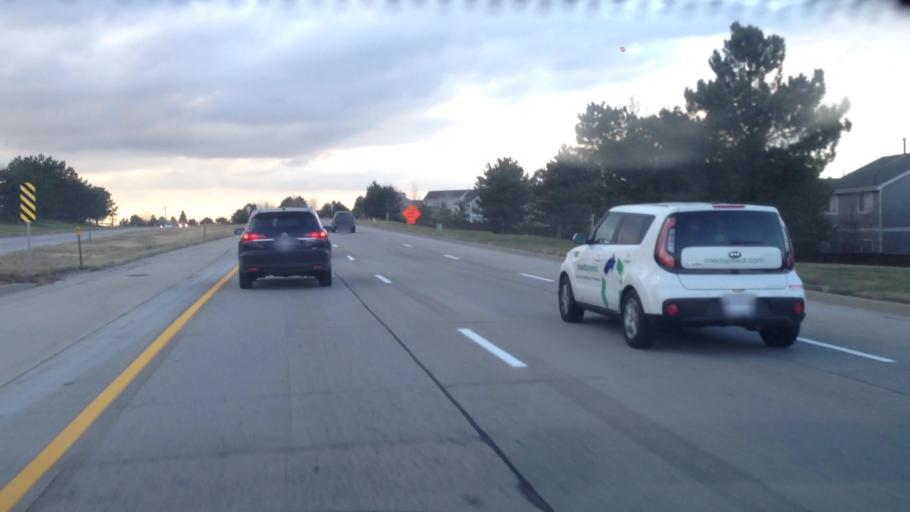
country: US
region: Colorado
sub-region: Douglas County
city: Stonegate
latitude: 39.5353
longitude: -104.8070
